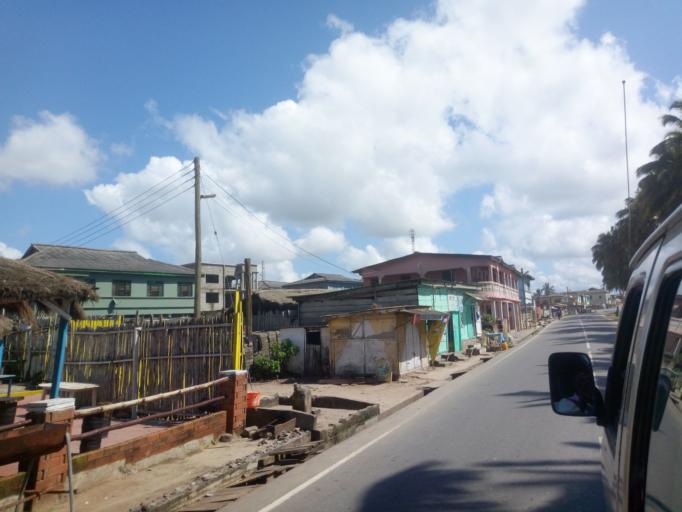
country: GH
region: Central
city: Elmina
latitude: 5.0895
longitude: -1.3470
